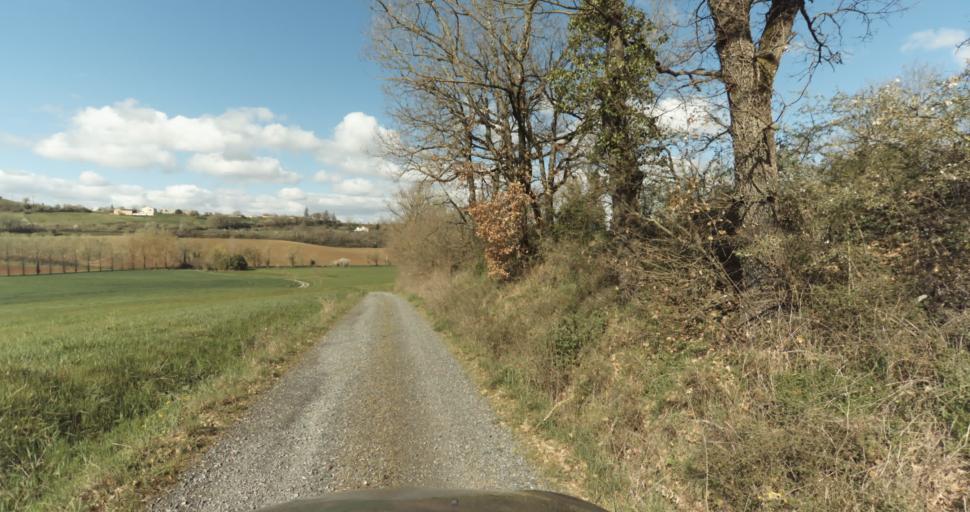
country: FR
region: Midi-Pyrenees
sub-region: Departement du Tarn
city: Puygouzon
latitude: 43.8740
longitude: 2.1774
